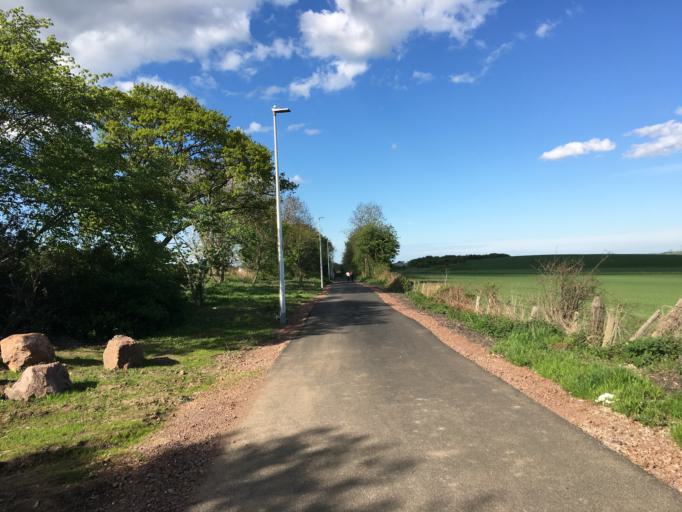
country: GB
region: Scotland
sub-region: Midlothian
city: Loanhead
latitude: 55.8956
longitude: -3.1320
